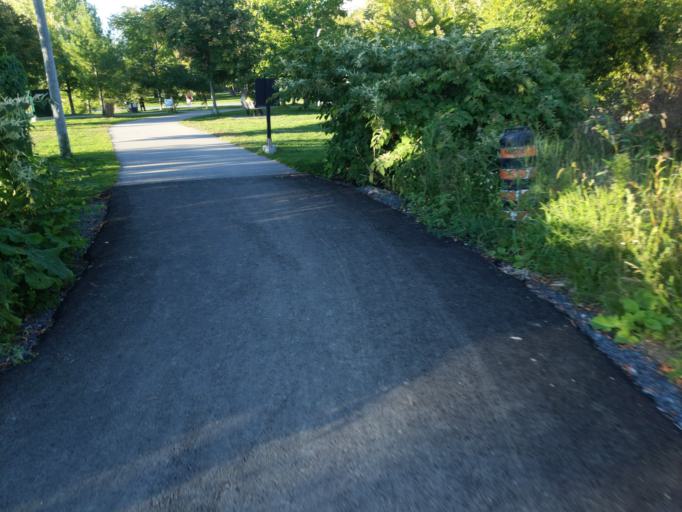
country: CA
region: Ontario
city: Ottawa
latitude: 45.4120
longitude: -75.6729
